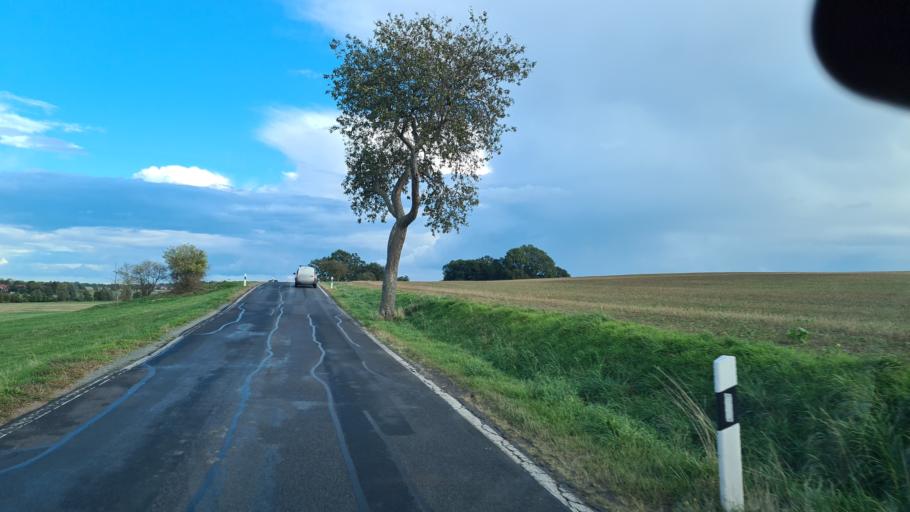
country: DE
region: Saxony
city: Dahlen
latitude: 51.3622
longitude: 13.0276
